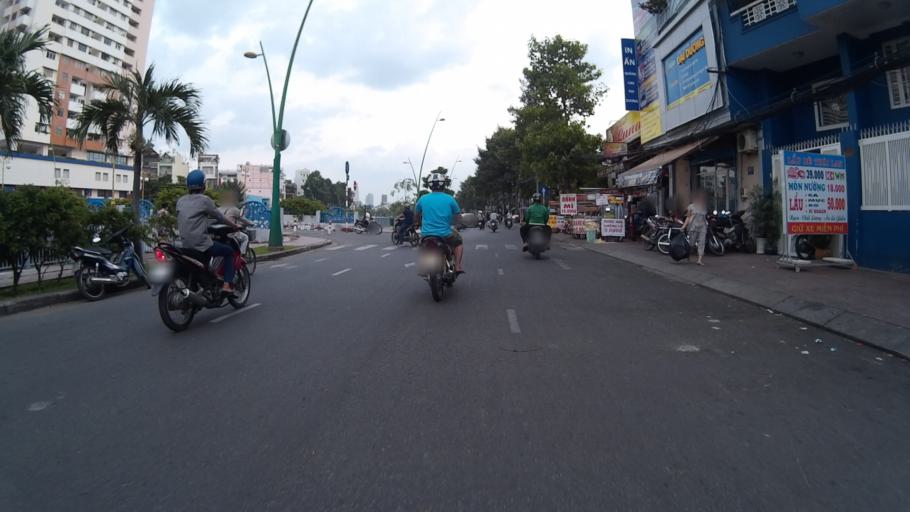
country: VN
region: Ho Chi Minh City
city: Quan Phu Nhuan
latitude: 10.7863
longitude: 106.6744
